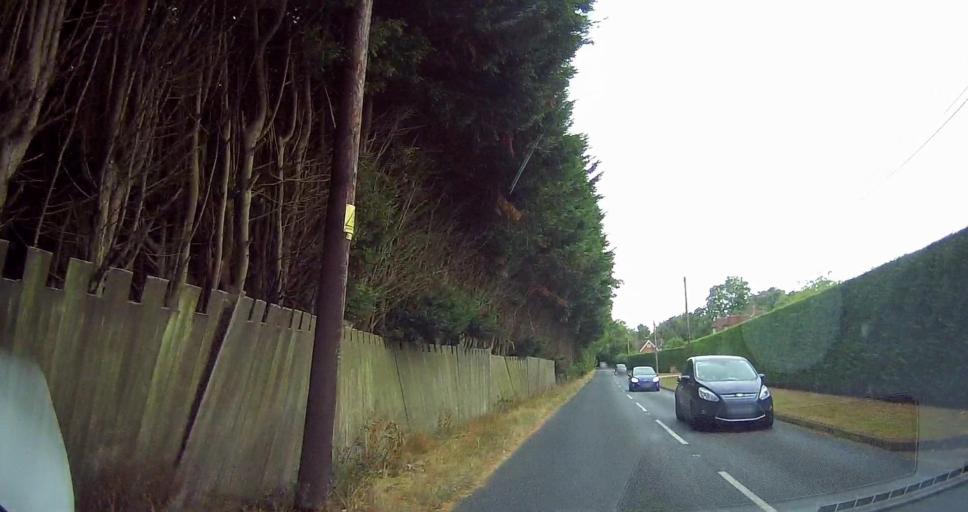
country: GB
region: England
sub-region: East Sussex
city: Wadhurst
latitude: 51.0796
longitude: 0.3715
